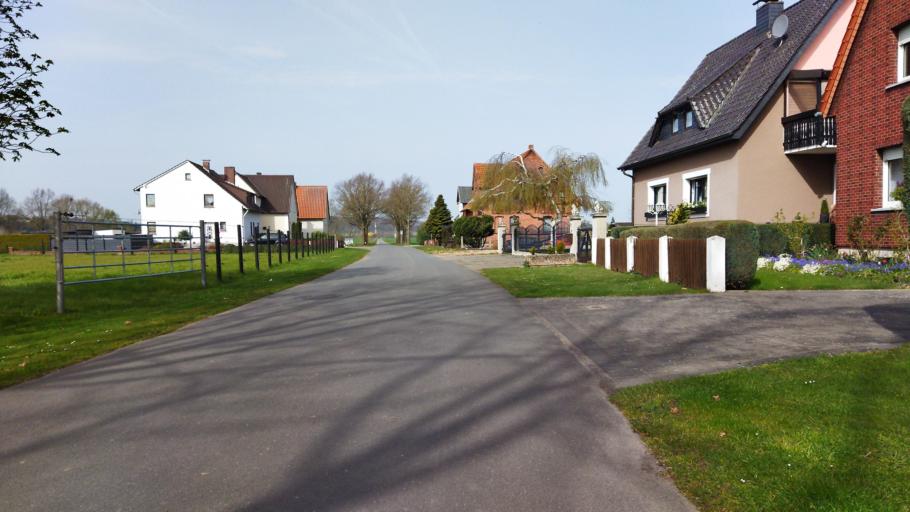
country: DE
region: North Rhine-Westphalia
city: Porta Westfalica
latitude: 52.1883
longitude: 8.9645
